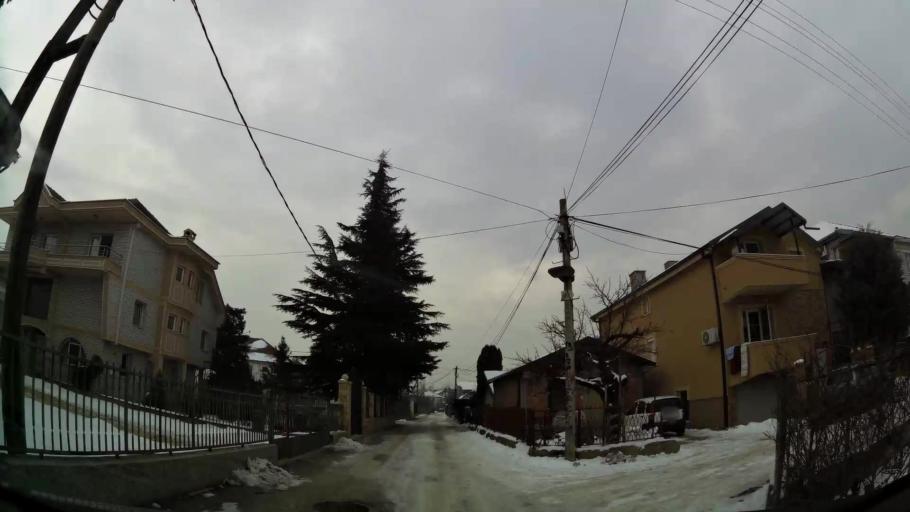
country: MK
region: Saraj
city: Saraj
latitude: 42.0345
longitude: 21.3537
